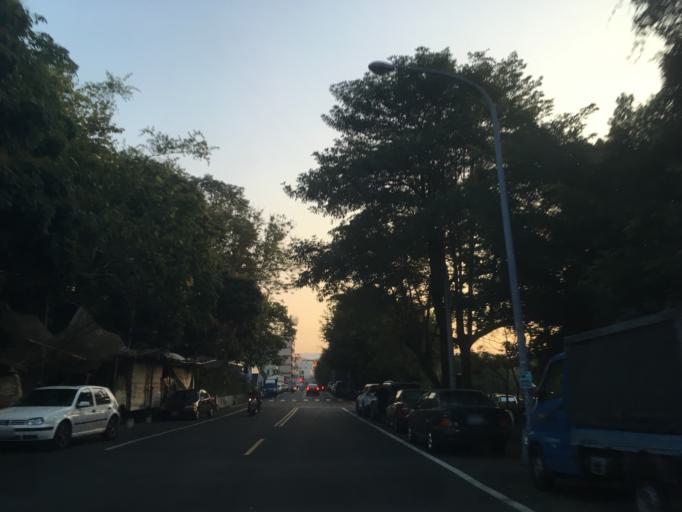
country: TW
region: Taiwan
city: Zhongxing New Village
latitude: 23.9823
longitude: 120.6889
